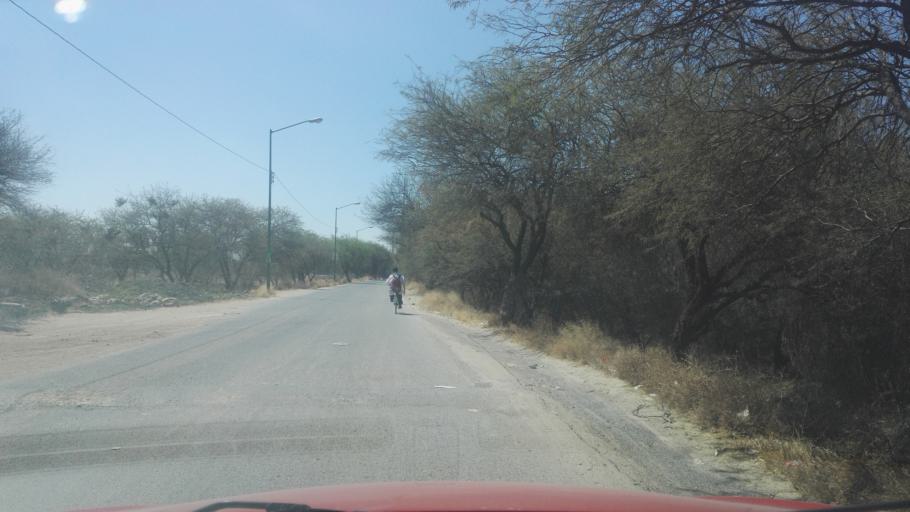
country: MX
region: Guanajuato
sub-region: Leon
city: Fraccionamiento Paraiso Real
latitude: 21.0784
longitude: -101.5978
